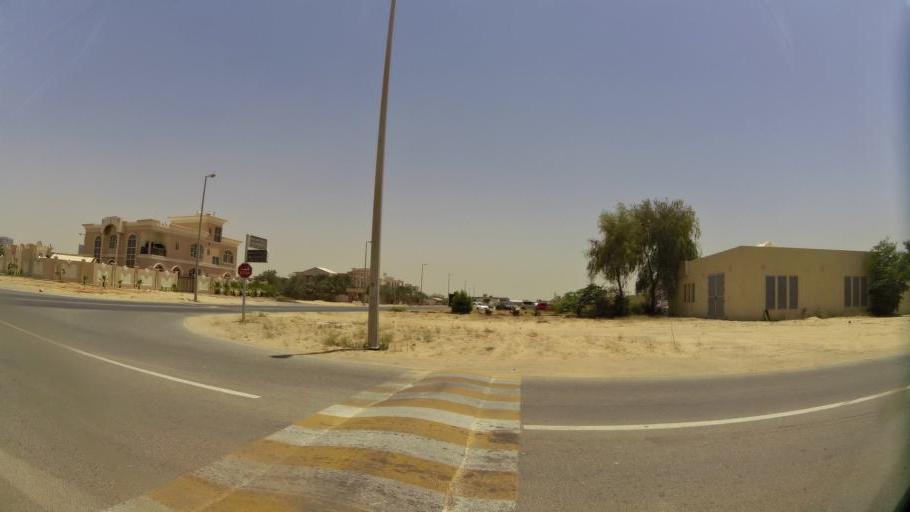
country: AE
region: Ajman
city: Ajman
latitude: 25.4084
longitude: 55.5004
